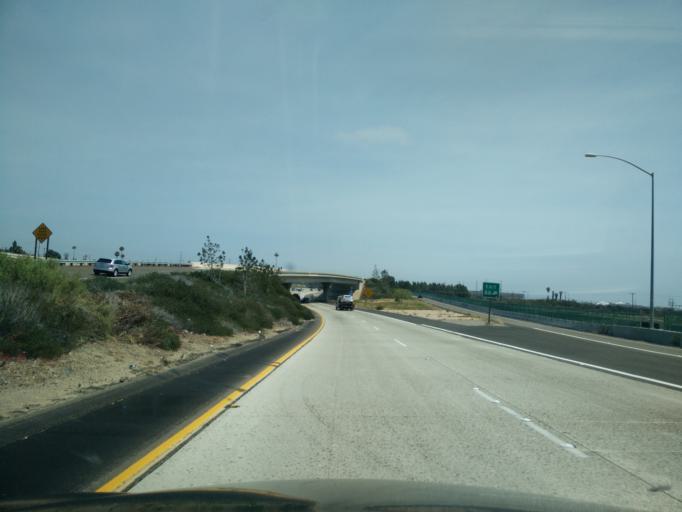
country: US
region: California
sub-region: San Diego County
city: Chula Vista
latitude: 32.6472
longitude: -117.1034
